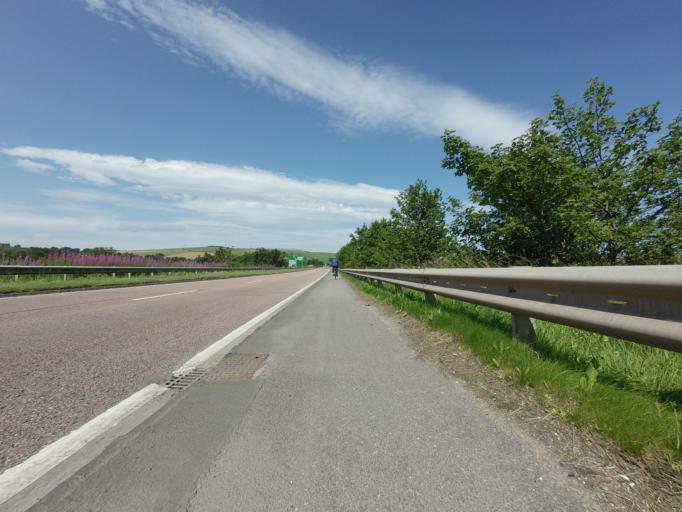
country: GB
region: Scotland
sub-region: Highland
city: Conon Bridge
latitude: 57.5720
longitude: -4.4290
